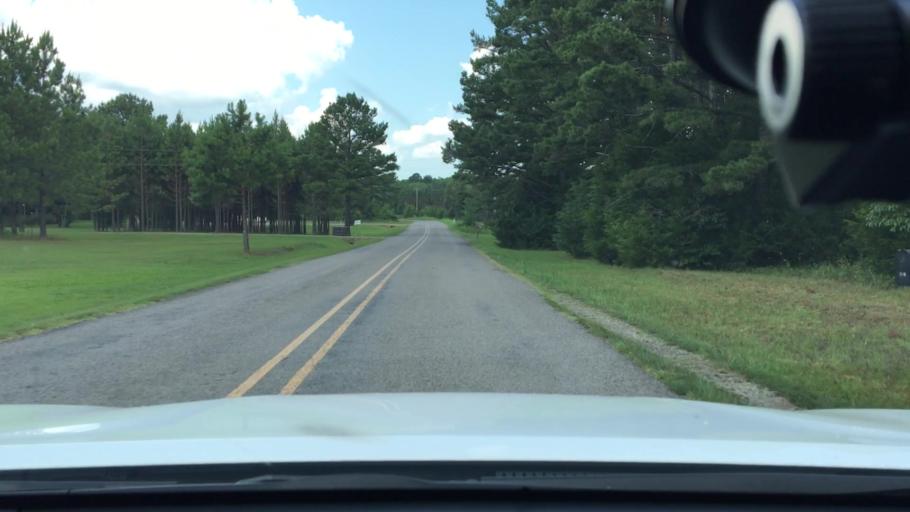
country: US
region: Arkansas
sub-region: Logan County
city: Paris
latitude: 35.2684
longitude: -93.6674
